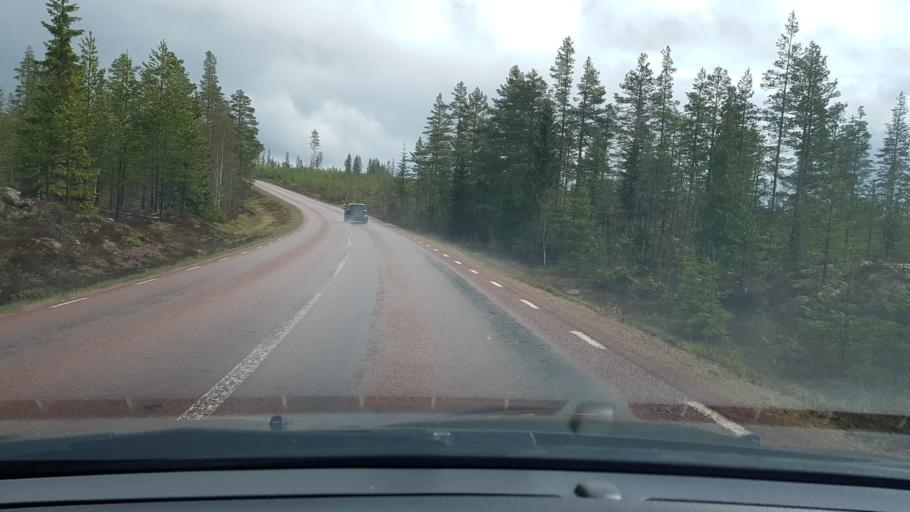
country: SE
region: Dalarna
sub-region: Malung-Saelens kommun
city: Malung
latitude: 61.0485
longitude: 13.3716
